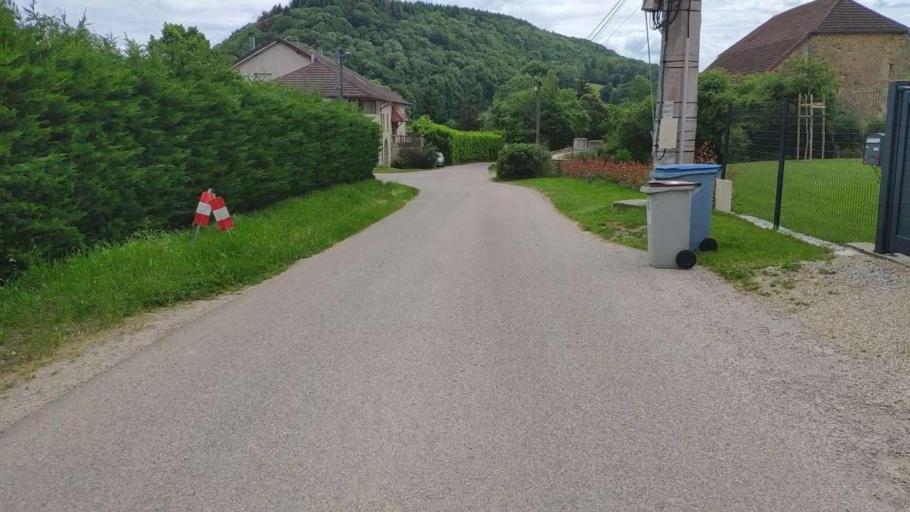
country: FR
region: Franche-Comte
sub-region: Departement du Jura
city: Montmorot
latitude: 46.7452
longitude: 5.5477
